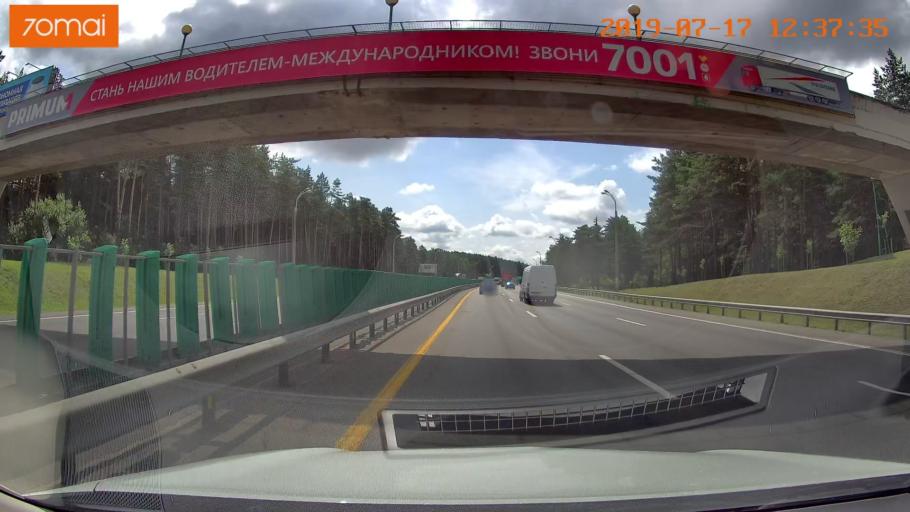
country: BY
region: Minsk
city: Vyaliki Trastsyanets
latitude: 53.8822
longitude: 27.6967
